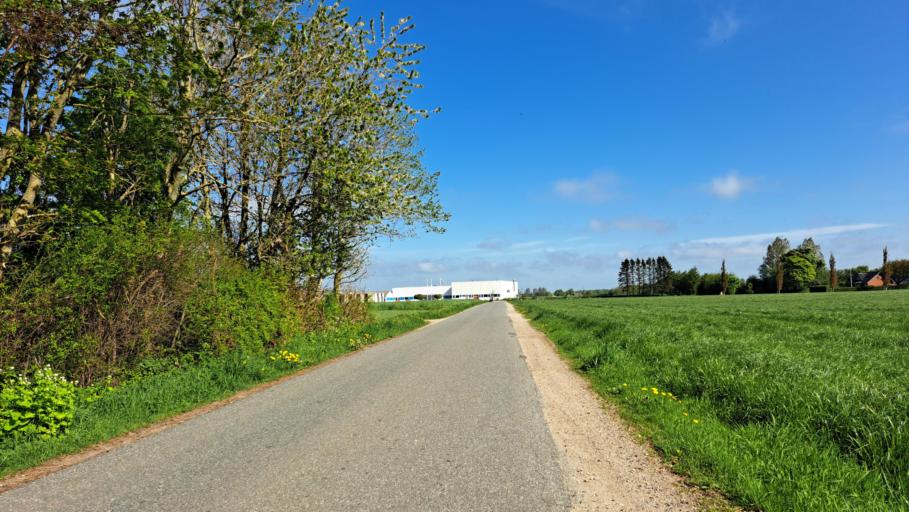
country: DK
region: Central Jutland
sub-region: Hedensted Kommune
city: Hedensted
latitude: 55.8036
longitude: 9.6554
